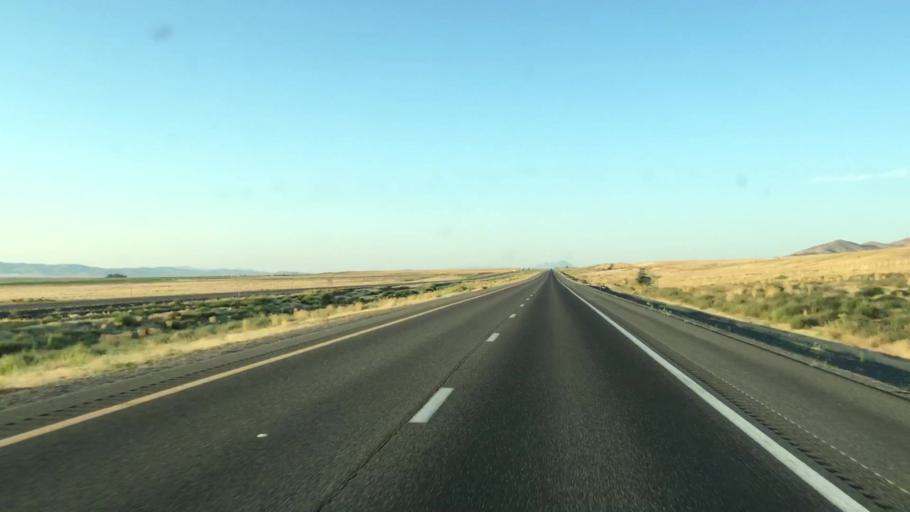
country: US
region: Nevada
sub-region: Humboldt County
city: Winnemucca
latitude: 40.7612
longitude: -118.0168
